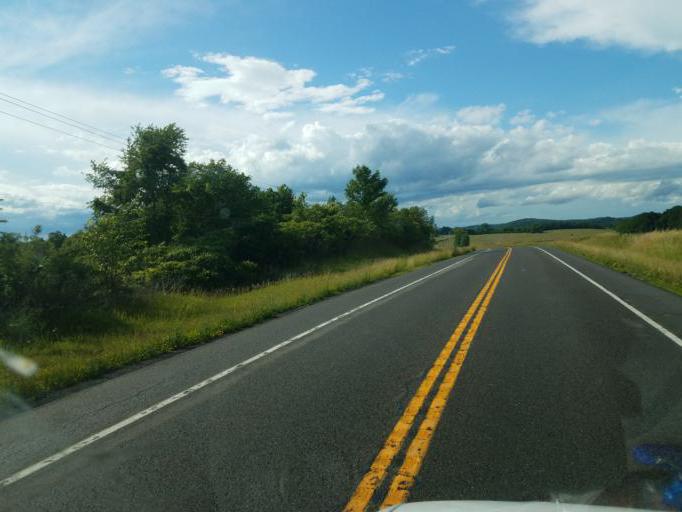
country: US
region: New York
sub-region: Wayne County
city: Clyde
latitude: 43.0044
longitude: -76.8549
